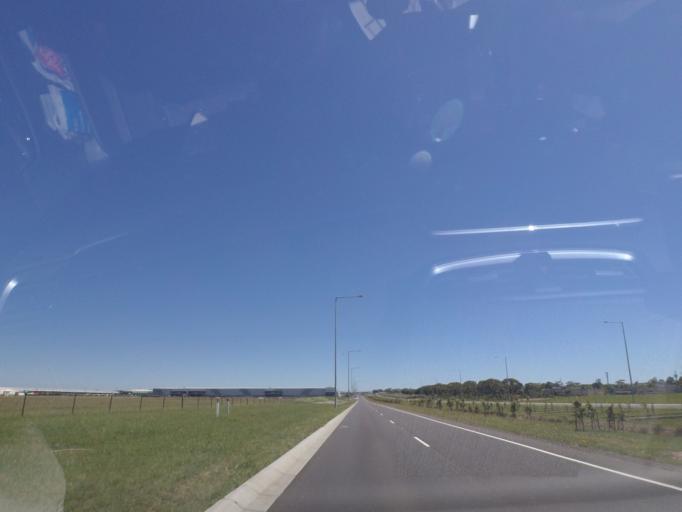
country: AU
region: Victoria
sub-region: Hume
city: Tullamarine
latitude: -37.7015
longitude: 144.8674
